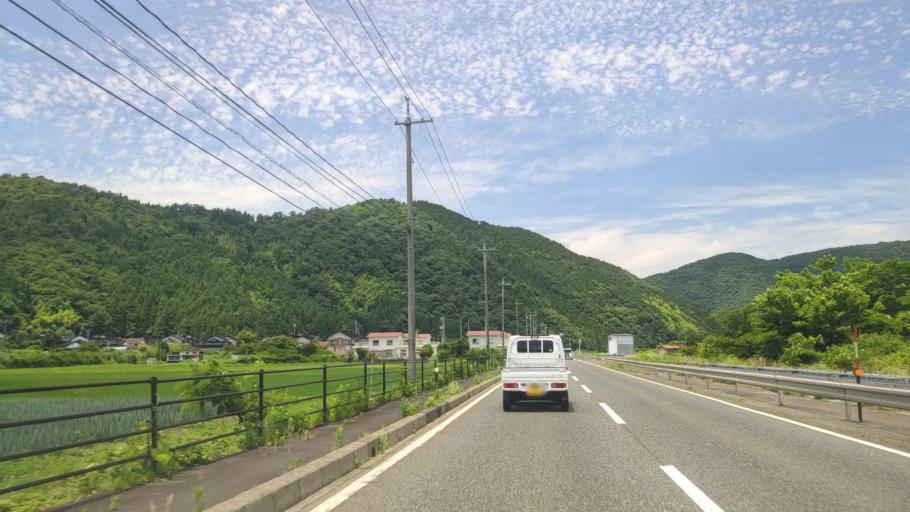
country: JP
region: Tottori
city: Tottori
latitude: 35.3552
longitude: 134.3831
